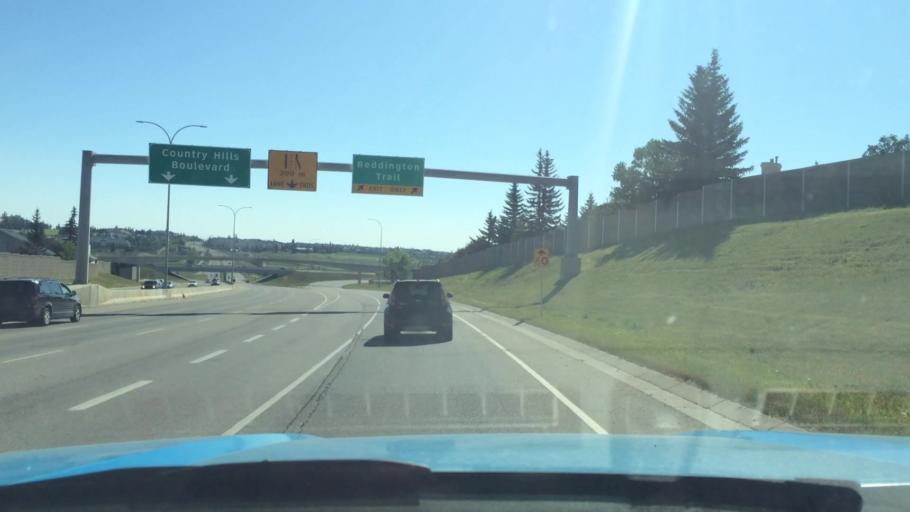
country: CA
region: Alberta
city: Calgary
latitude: 51.1423
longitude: -114.0996
